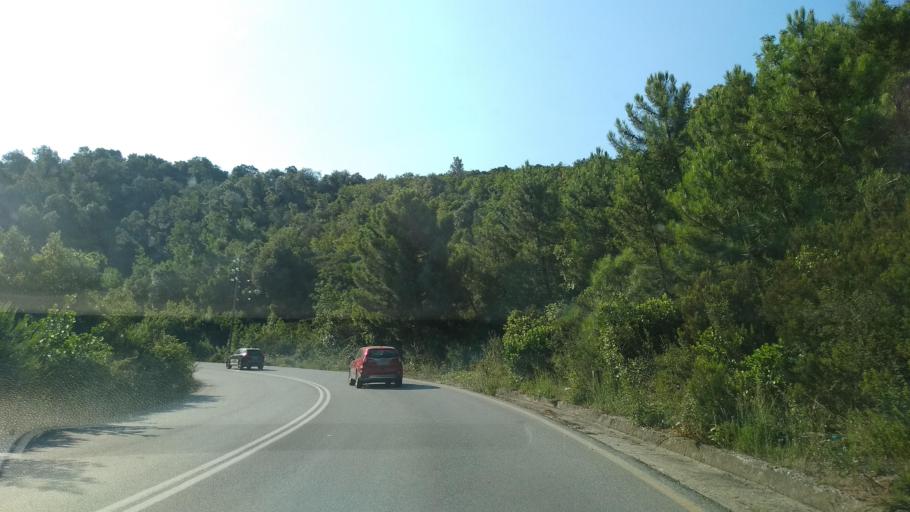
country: GR
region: Central Macedonia
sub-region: Nomos Chalkidikis
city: Stratonion
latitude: 40.5788
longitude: 23.8119
